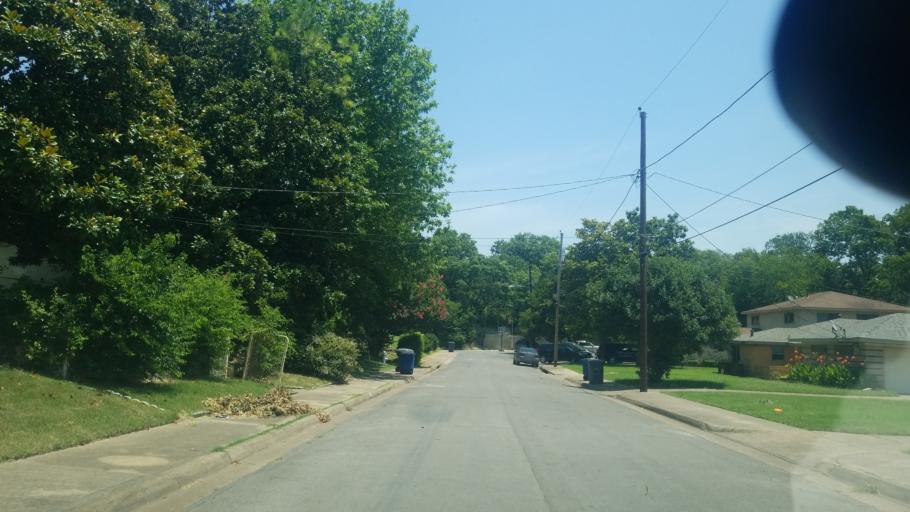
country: US
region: Texas
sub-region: Dallas County
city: Dallas
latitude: 32.7311
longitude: -96.7912
